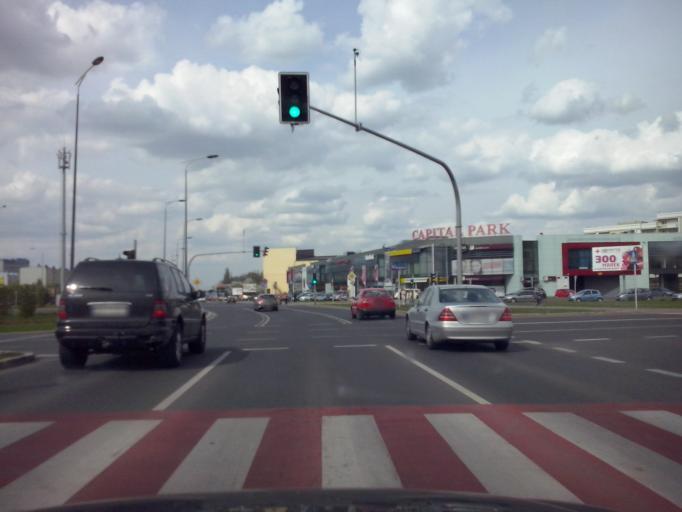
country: PL
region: Subcarpathian Voivodeship
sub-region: Rzeszow
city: Rzeszow
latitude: 50.0280
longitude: 22.0173
